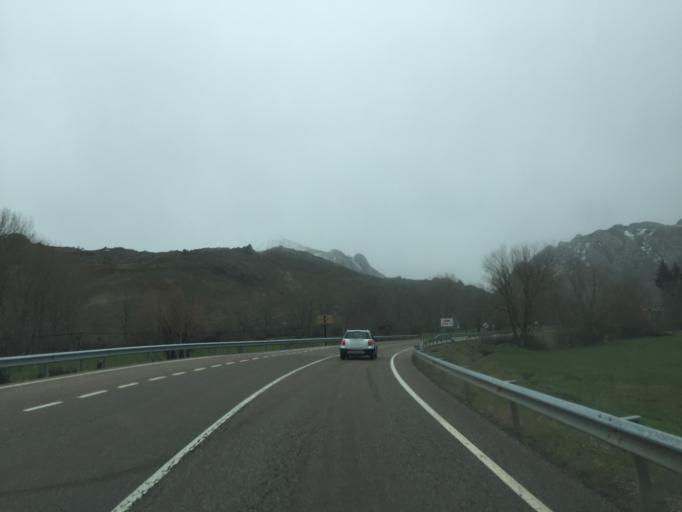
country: ES
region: Castille and Leon
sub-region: Provincia de Leon
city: San Emiliano
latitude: 42.9483
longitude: -5.9999
